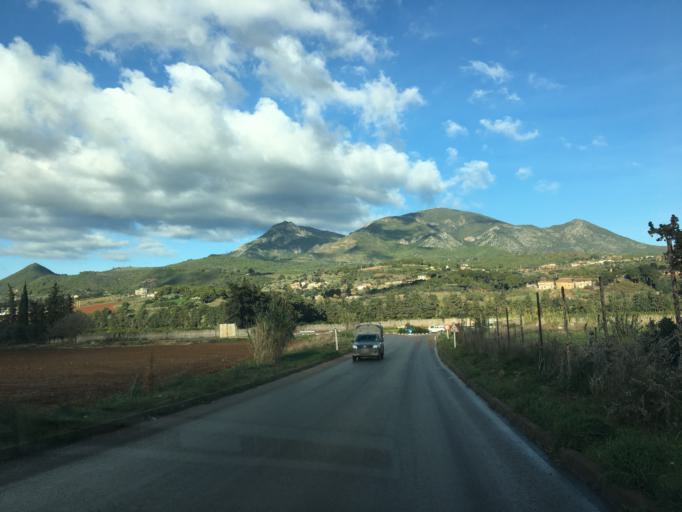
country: DZ
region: Tipaza
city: Tipasa
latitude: 36.5711
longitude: 2.4061
